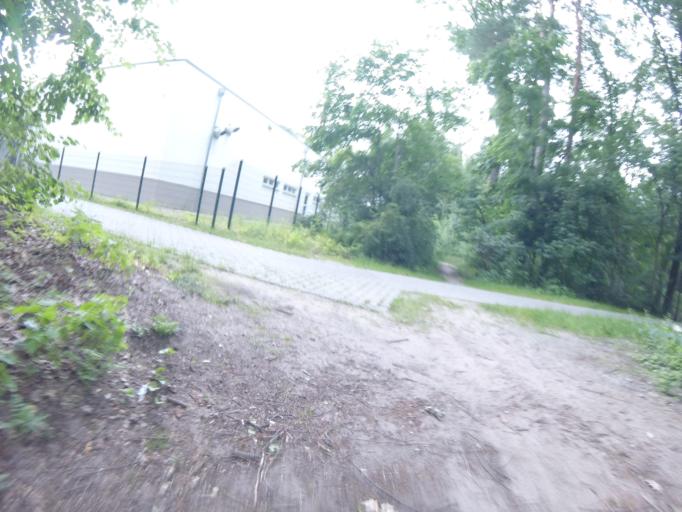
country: DE
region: Brandenburg
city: Bestensee
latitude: 52.2431
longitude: 13.6449
